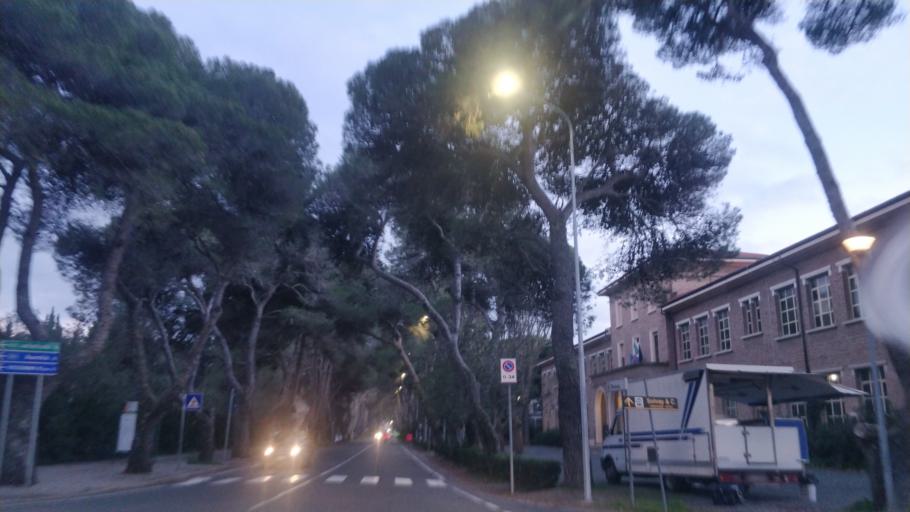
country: IT
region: Tuscany
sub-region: Provincia di Livorno
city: Rosignano Solvay-Castiglioncello
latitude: 43.3915
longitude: 10.4397
